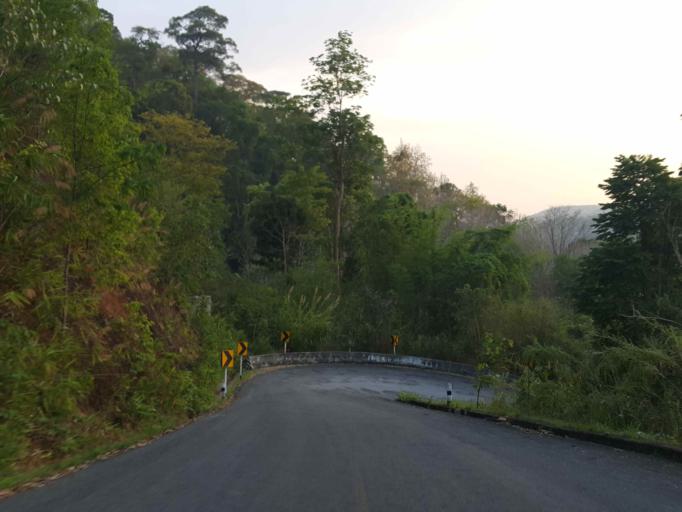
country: TH
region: Chiang Mai
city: Mae On
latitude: 19.0126
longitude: 99.3018
